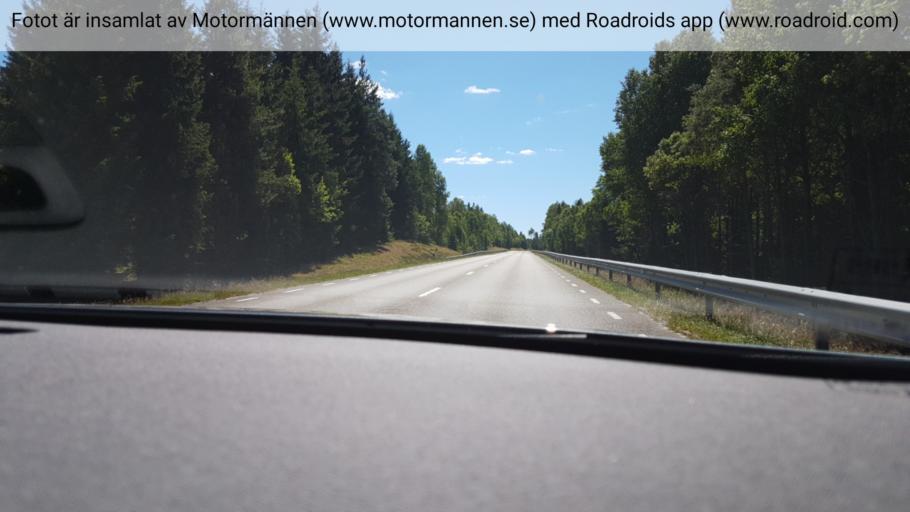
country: SE
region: Joenkoeping
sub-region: Gnosjo Kommun
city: Marieholm
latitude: 57.6235
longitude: 13.7731
